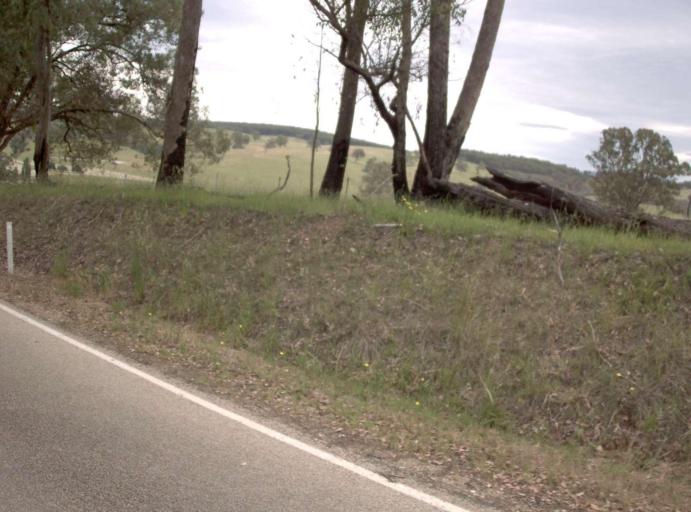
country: AU
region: Victoria
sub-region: East Gippsland
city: Bairnsdale
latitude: -37.7401
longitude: 147.3132
